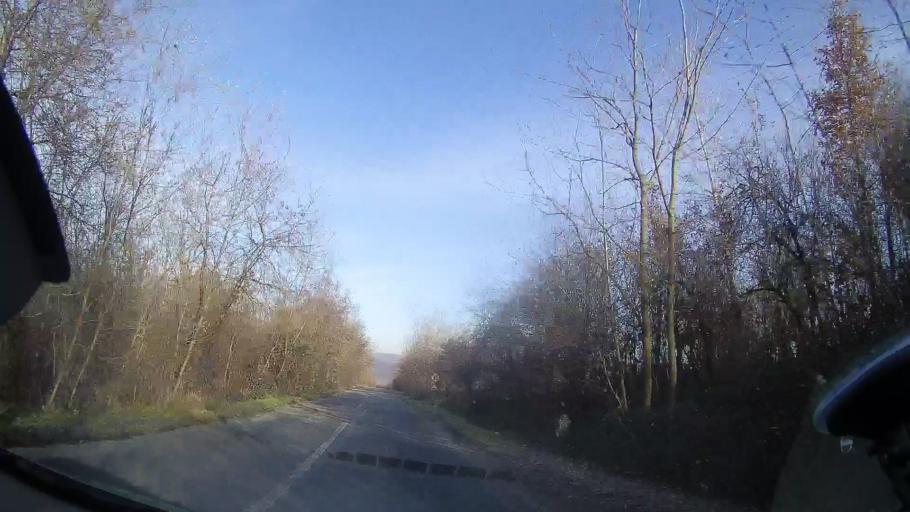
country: RO
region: Bihor
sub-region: Comuna Brusturi
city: Brusturi
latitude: 47.1159
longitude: 22.2638
